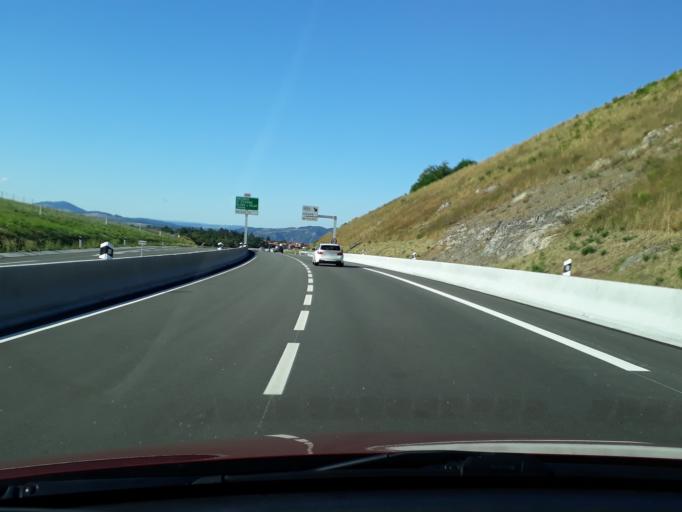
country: FR
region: Auvergne
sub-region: Departement de la Haute-Loire
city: Vals-pres-le-Puy
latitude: 45.0212
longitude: 3.9011
